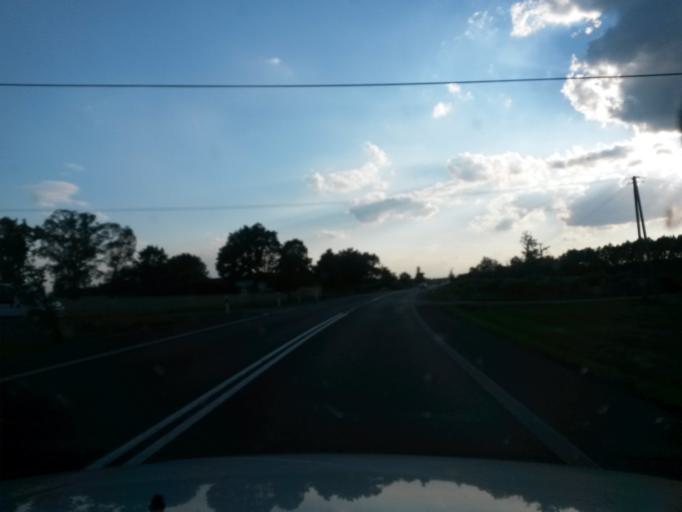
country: PL
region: Lodz Voivodeship
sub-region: Powiat belchatowski
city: Rusiec
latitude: 51.3166
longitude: 18.9513
